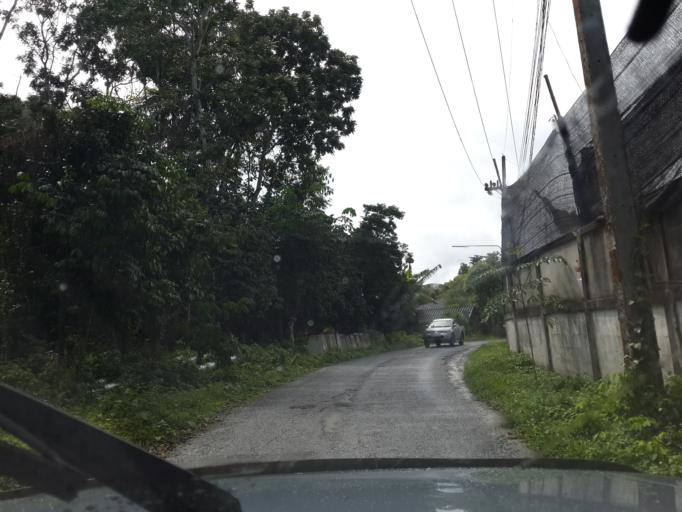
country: TH
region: Narathiwat
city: Rueso
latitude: 6.3862
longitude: 101.5155
